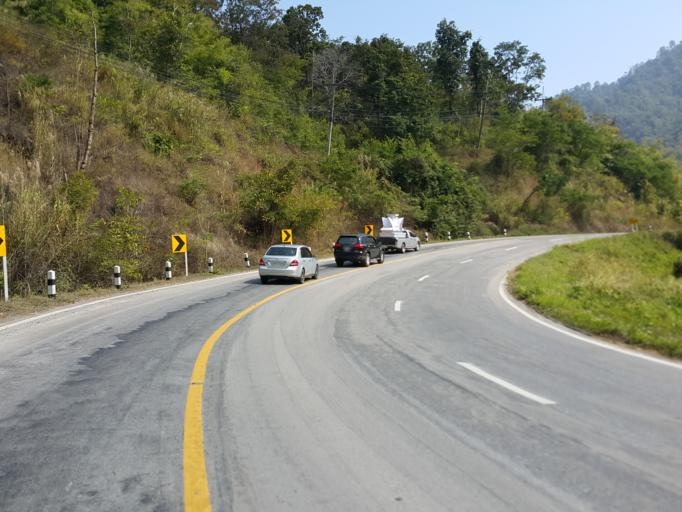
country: TH
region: Lampang
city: Wang Nuea
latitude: 19.0949
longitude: 99.4293
